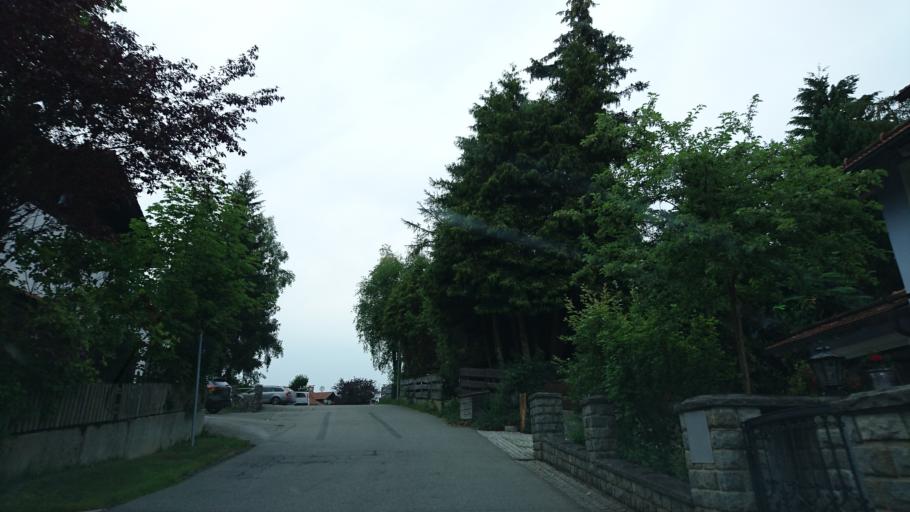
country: DE
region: Bavaria
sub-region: Lower Bavaria
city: Neuschonau
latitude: 48.8818
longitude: 13.4708
